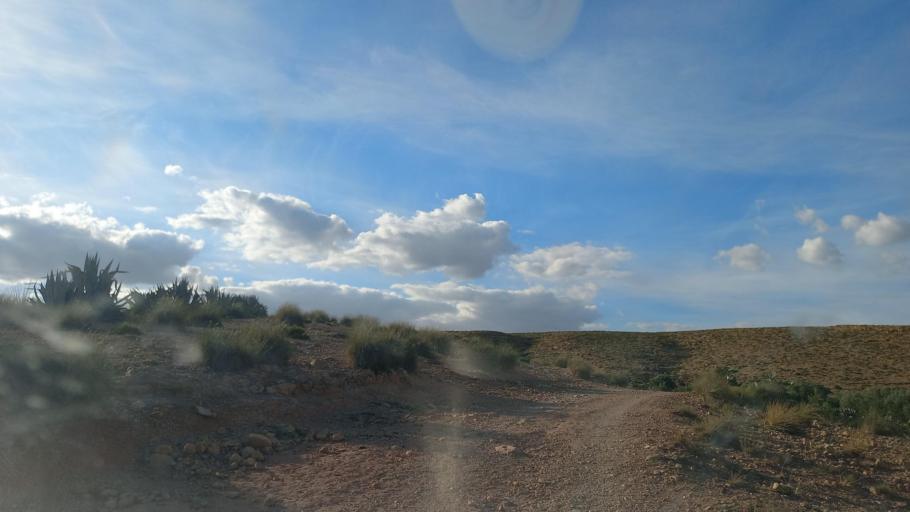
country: TN
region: Al Qasrayn
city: Sbiba
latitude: 35.3805
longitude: 9.0166
